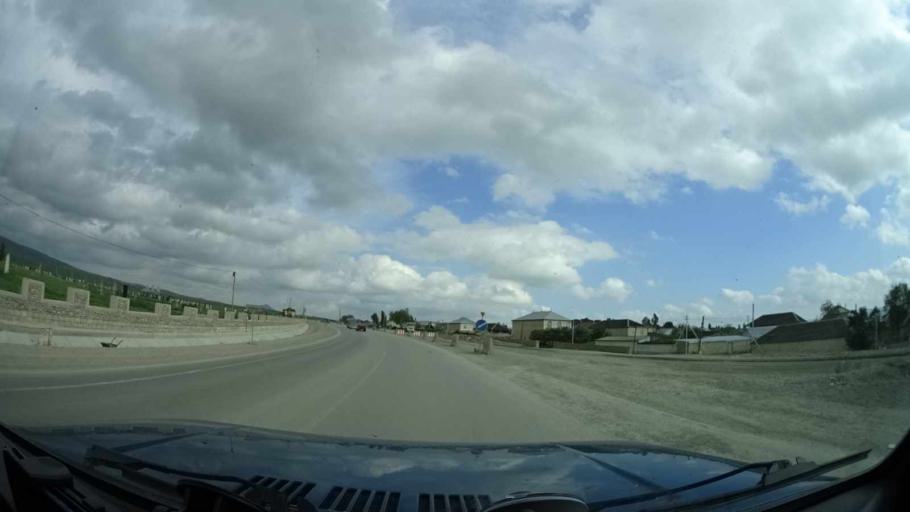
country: AZ
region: Samaxi
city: Shamakhi
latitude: 40.5921
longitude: 48.7041
